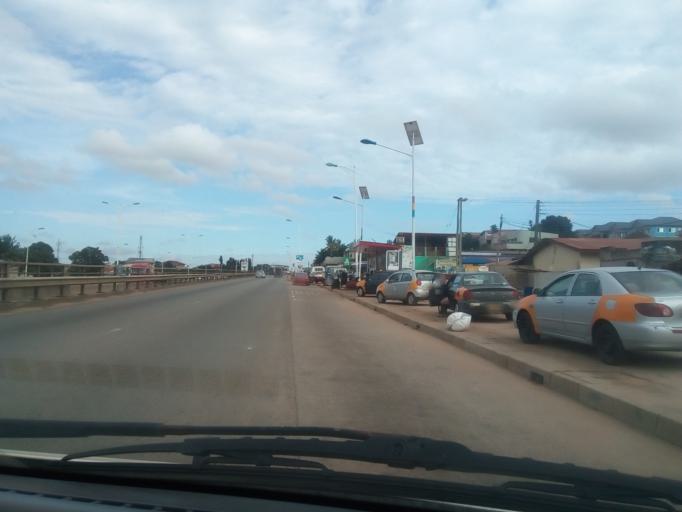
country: GH
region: Greater Accra
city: Dome
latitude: 5.6484
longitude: -0.2513
